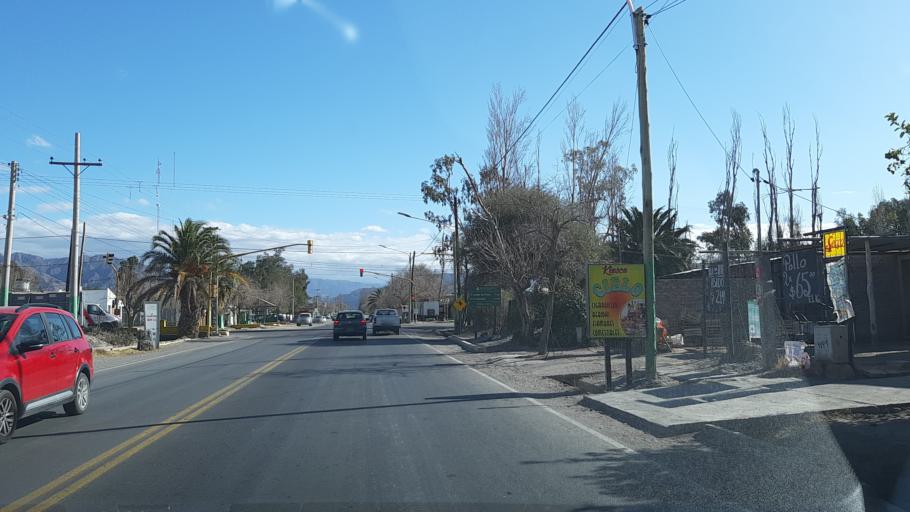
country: AR
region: San Juan
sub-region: Departamento de Rivadavia
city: Rivadavia
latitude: -31.5395
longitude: -68.6151
